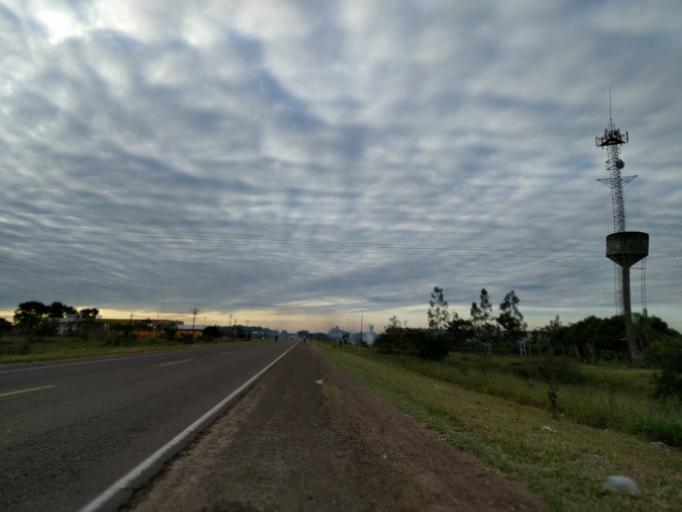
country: BO
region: Santa Cruz
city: Santa Rita
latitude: -17.8854
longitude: -63.2649
